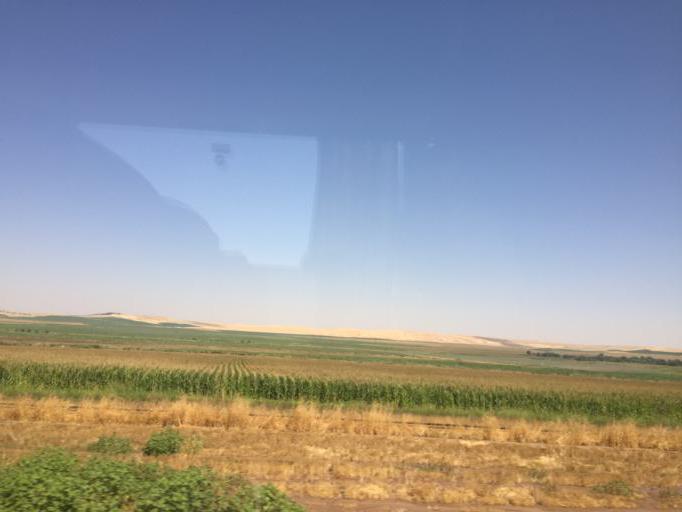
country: TR
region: Diyarbakir
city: Tepe
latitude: 37.8493
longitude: 40.7910
